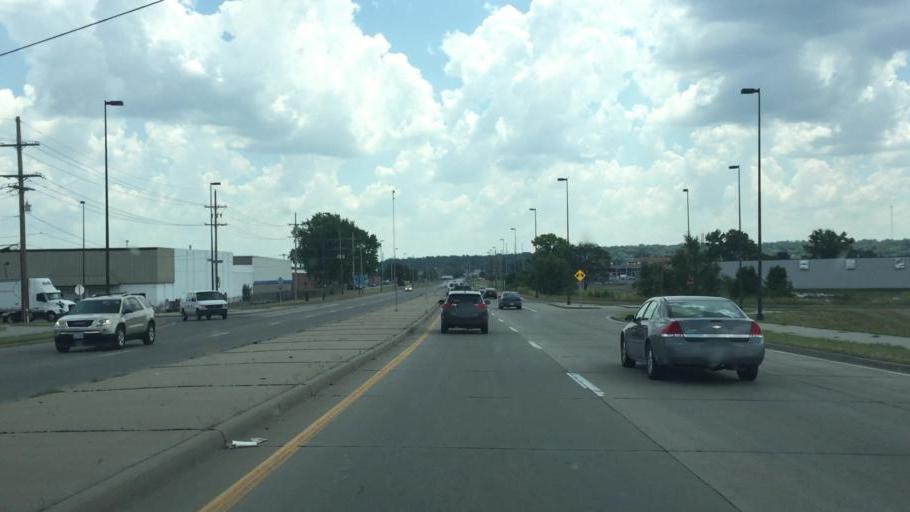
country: US
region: Missouri
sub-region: Clay County
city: North Kansas City
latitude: 39.1383
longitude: -94.5295
